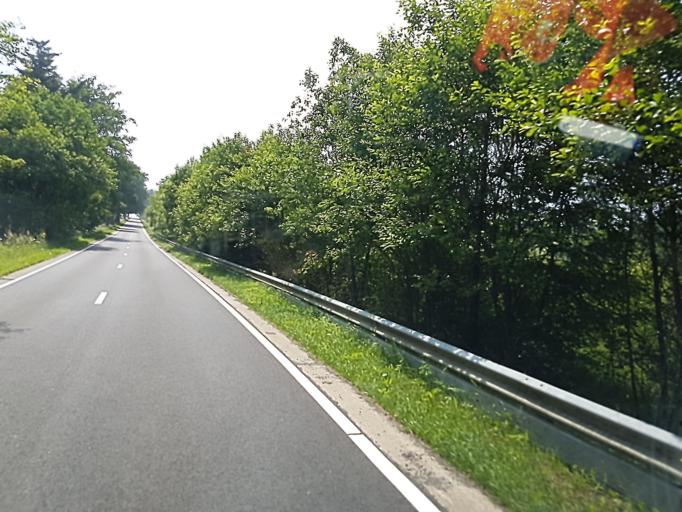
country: BE
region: Wallonia
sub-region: Province de Liege
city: Lierneux
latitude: 50.3375
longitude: 5.7877
